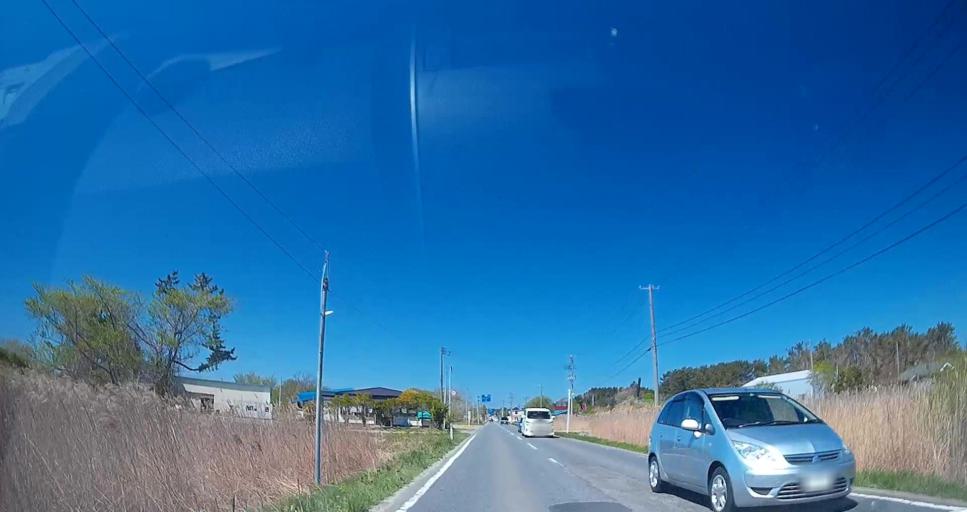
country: JP
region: Aomori
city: Misawa
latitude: 40.8456
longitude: 141.3741
